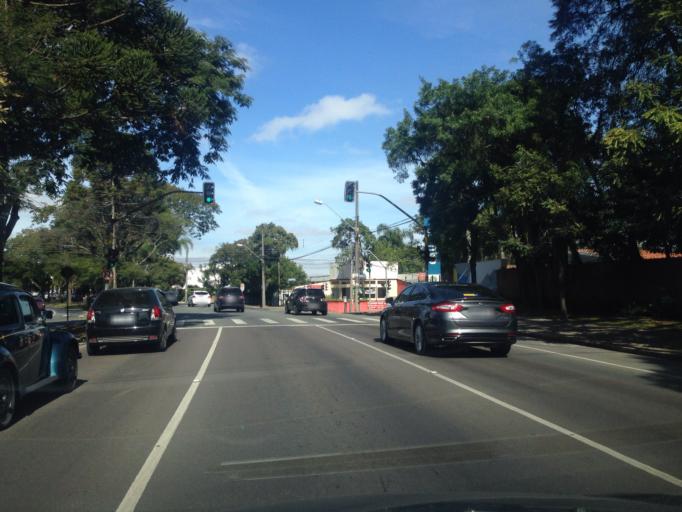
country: BR
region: Parana
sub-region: Curitiba
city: Curitiba
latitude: -25.4243
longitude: -49.2425
